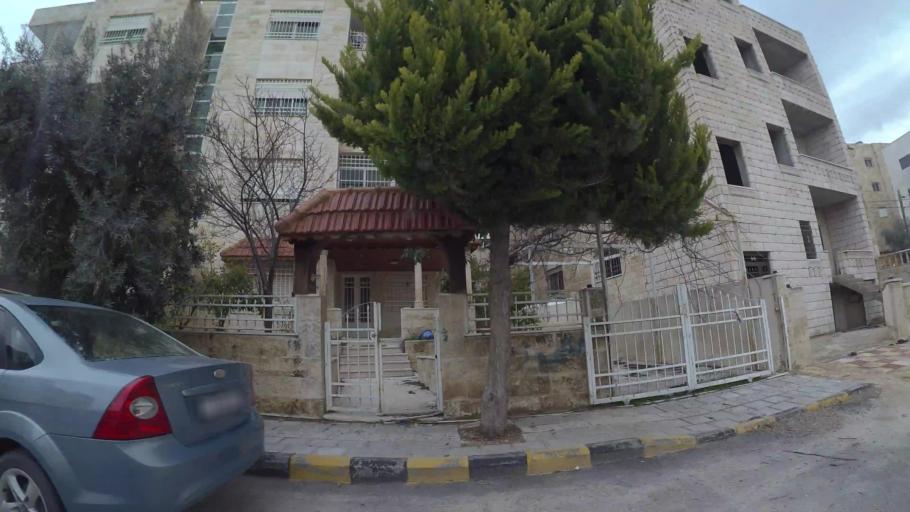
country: JO
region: Amman
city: Umm as Summaq
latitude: 31.8995
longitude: 35.8458
